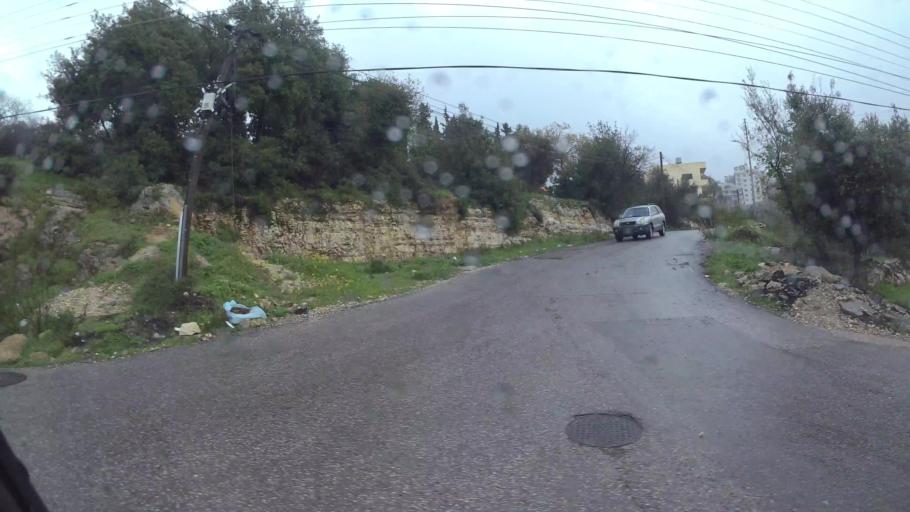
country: JO
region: Amman
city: Wadi as Sir
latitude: 32.0100
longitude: 35.7956
